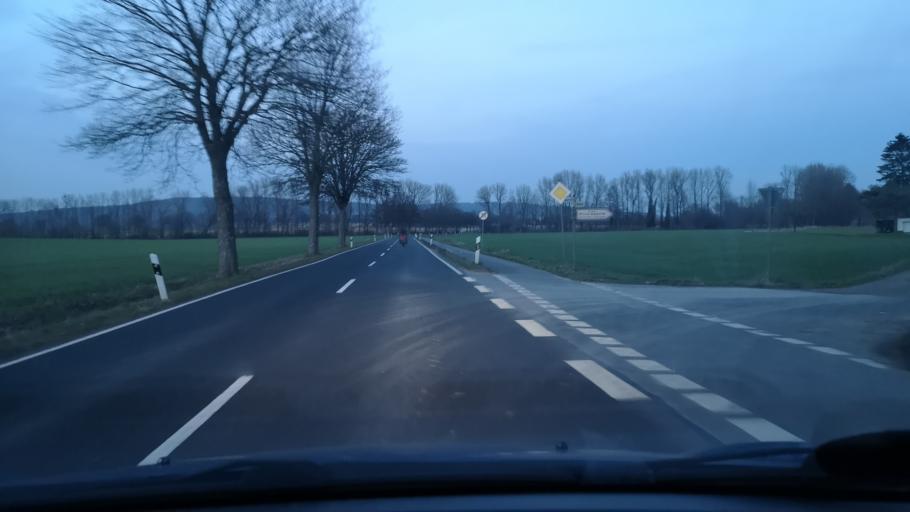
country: DE
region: Lower Saxony
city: Salzhemmendorf
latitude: 52.0742
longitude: 9.5883
